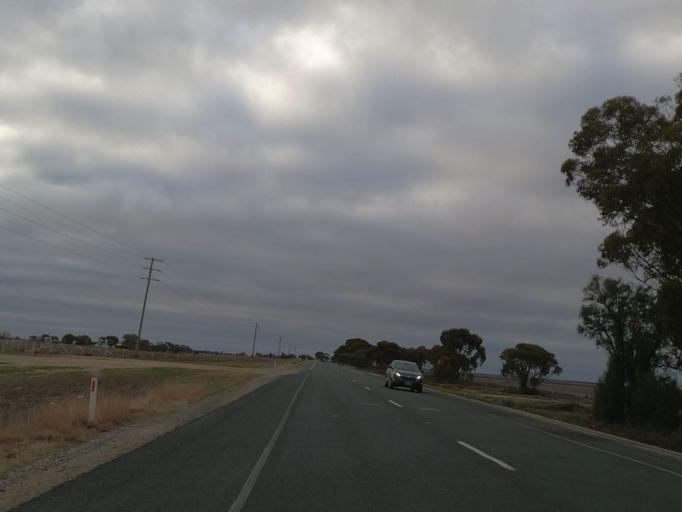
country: AU
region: Victoria
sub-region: Swan Hill
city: Swan Hill
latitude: -35.5817
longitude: 143.7895
